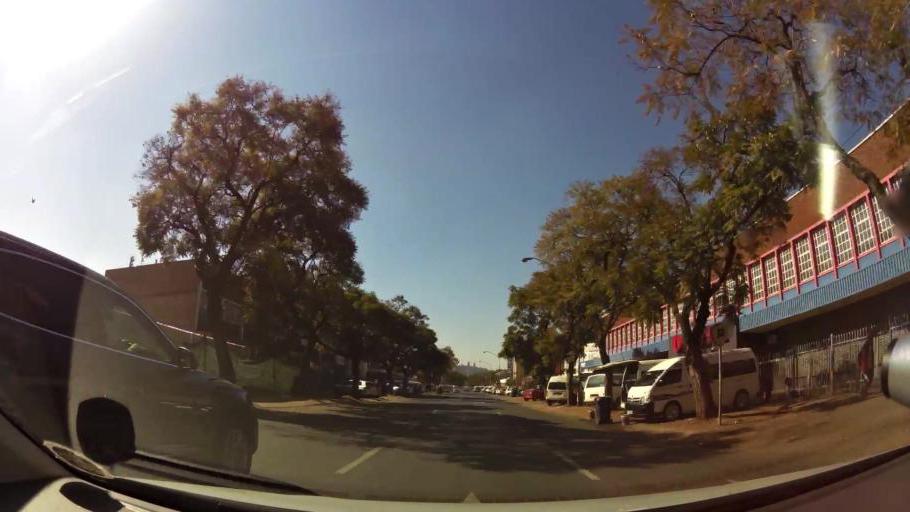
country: ZA
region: Gauteng
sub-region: City of Tshwane Metropolitan Municipality
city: Pretoria
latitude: -25.7418
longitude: 28.1905
